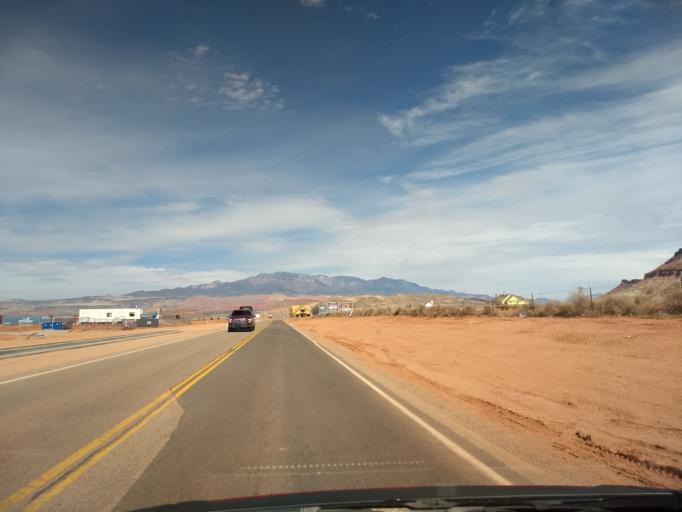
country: US
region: Utah
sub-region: Washington County
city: Washington
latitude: 37.0608
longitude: -113.4902
